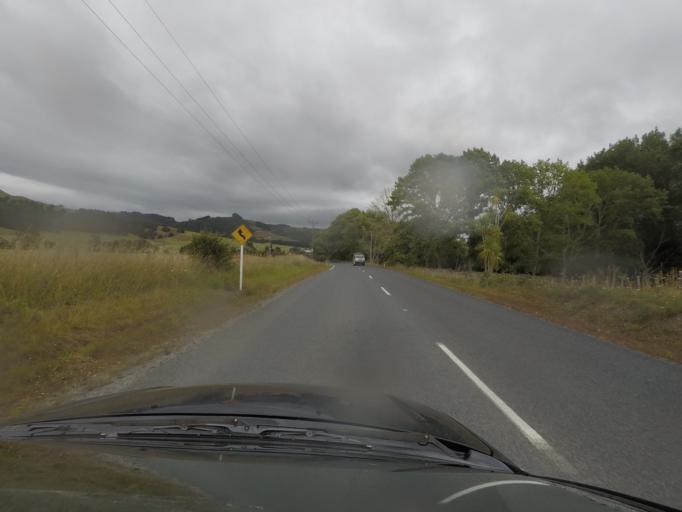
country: NZ
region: Auckland
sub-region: Auckland
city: Warkworth
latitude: -36.2867
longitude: 174.6620
